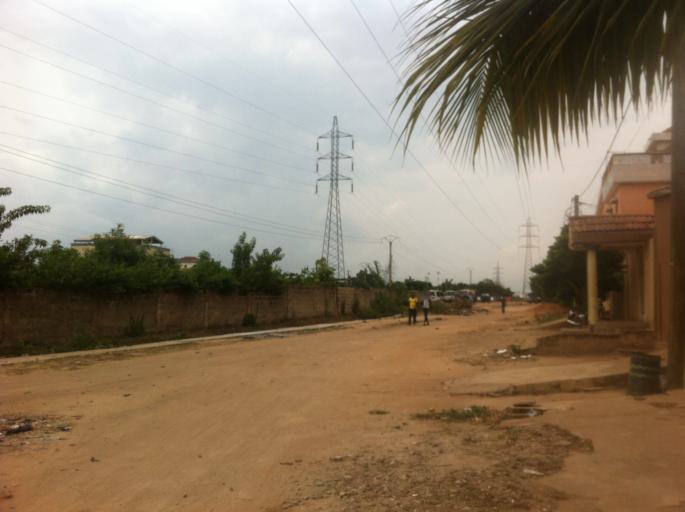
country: TG
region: Maritime
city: Lome
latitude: 6.1843
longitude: 1.2038
